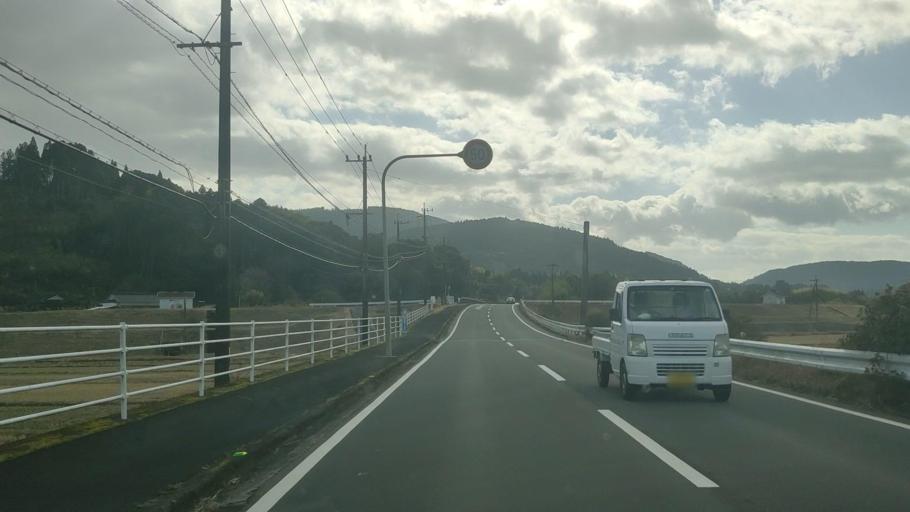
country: JP
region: Kagoshima
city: Okuchi-shinohara
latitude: 31.9956
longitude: 130.7485
